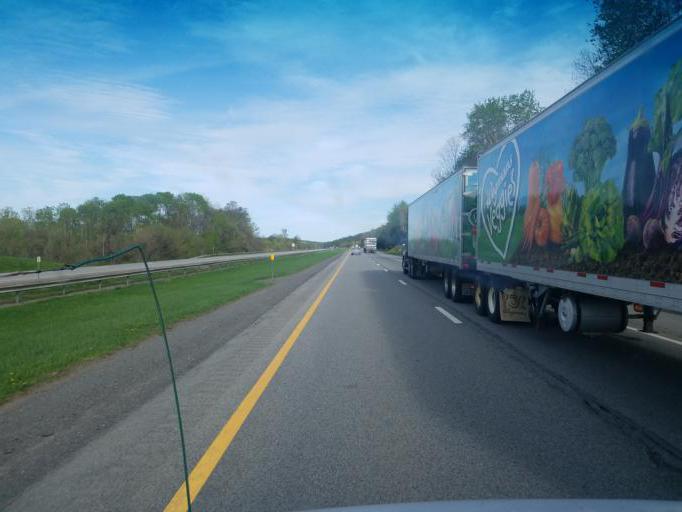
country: US
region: New York
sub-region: Herkimer County
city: Little Falls
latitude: 43.0104
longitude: -74.9143
